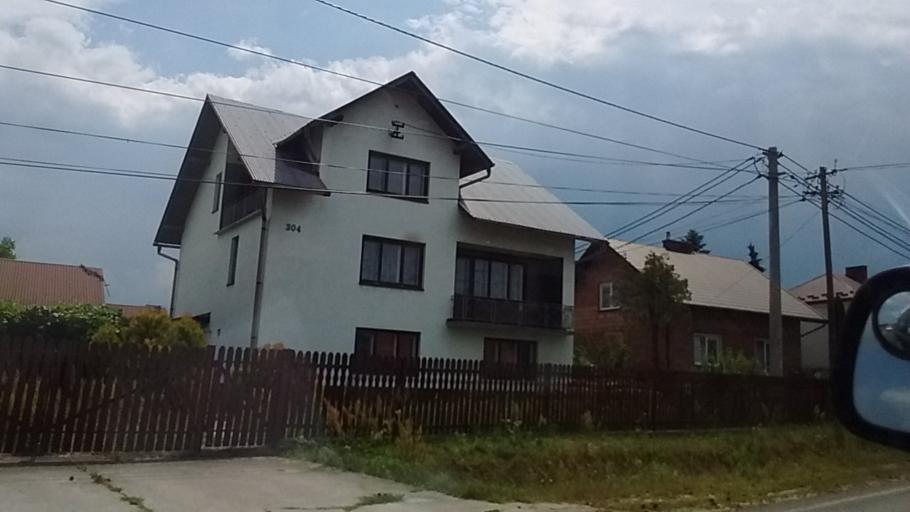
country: PL
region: Subcarpathian Voivodeship
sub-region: Powiat lezajski
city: Giedlarowa
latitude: 50.2275
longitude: 22.4031
